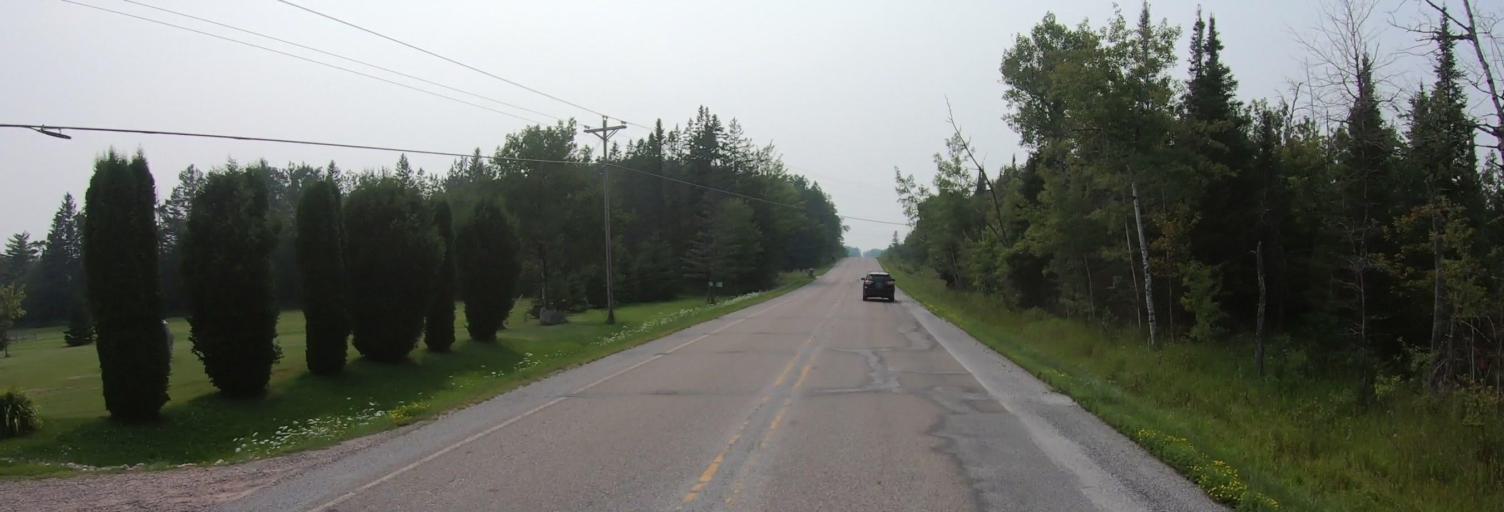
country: US
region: Michigan
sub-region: Chippewa County
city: Sault Ste. Marie
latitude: 46.4628
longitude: -84.3126
